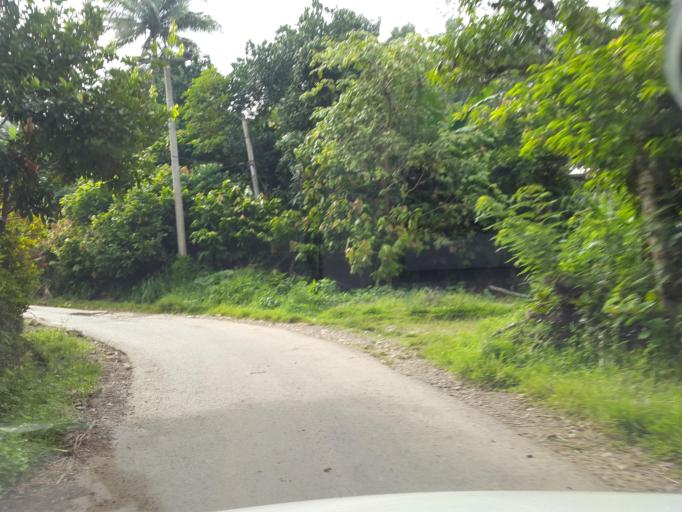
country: ID
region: South Sulawesi
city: Makale
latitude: -3.0315
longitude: 119.8472
